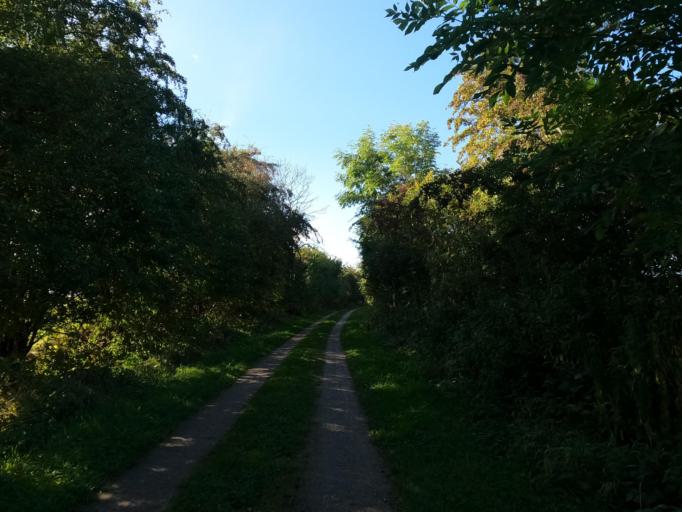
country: DE
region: Schleswig-Holstein
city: Grossenbrode
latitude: 54.3582
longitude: 11.0462
